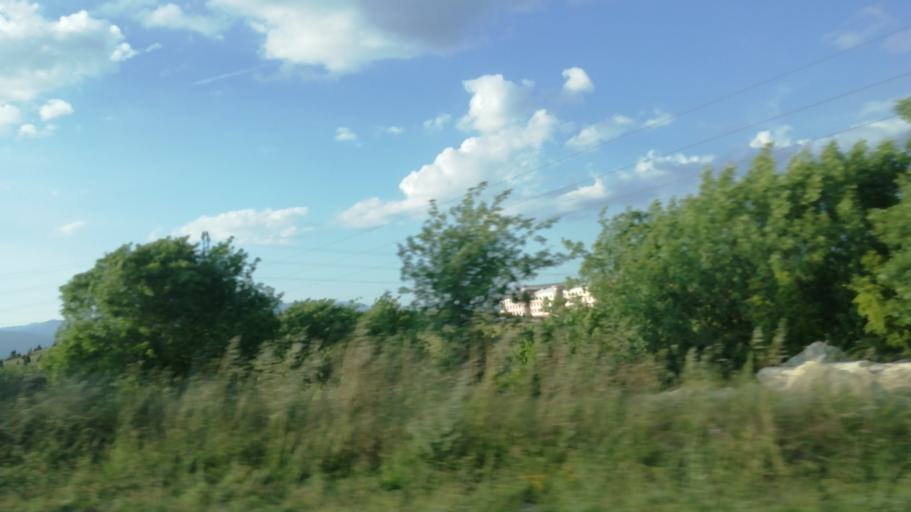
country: TR
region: Karabuk
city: Karabuk
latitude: 41.1327
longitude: 32.6273
